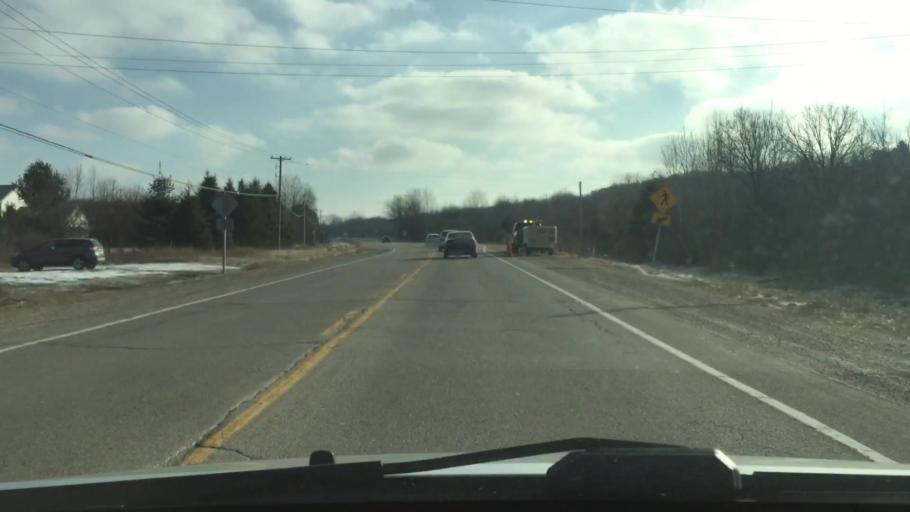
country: US
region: Wisconsin
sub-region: Waukesha County
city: Wales
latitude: 43.0131
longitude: -88.3993
